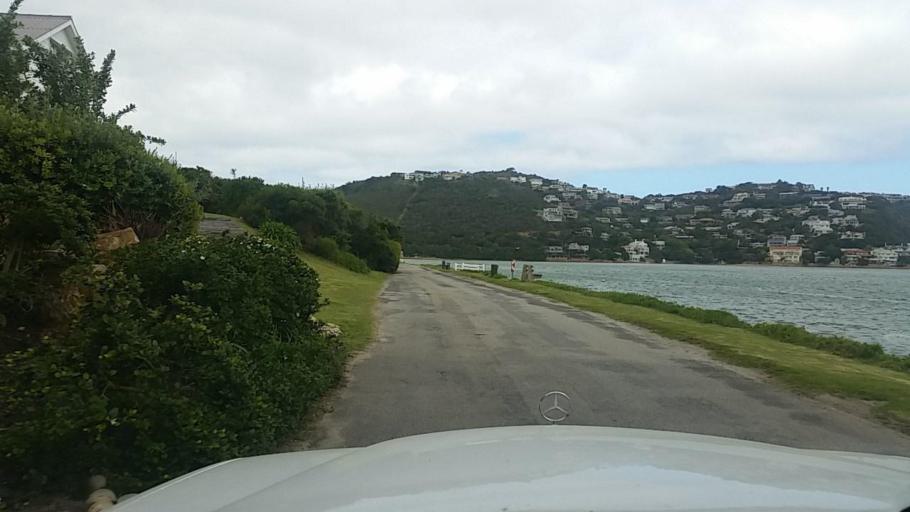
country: ZA
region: Western Cape
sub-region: Eden District Municipality
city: Knysna
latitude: -34.0692
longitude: 23.0588
